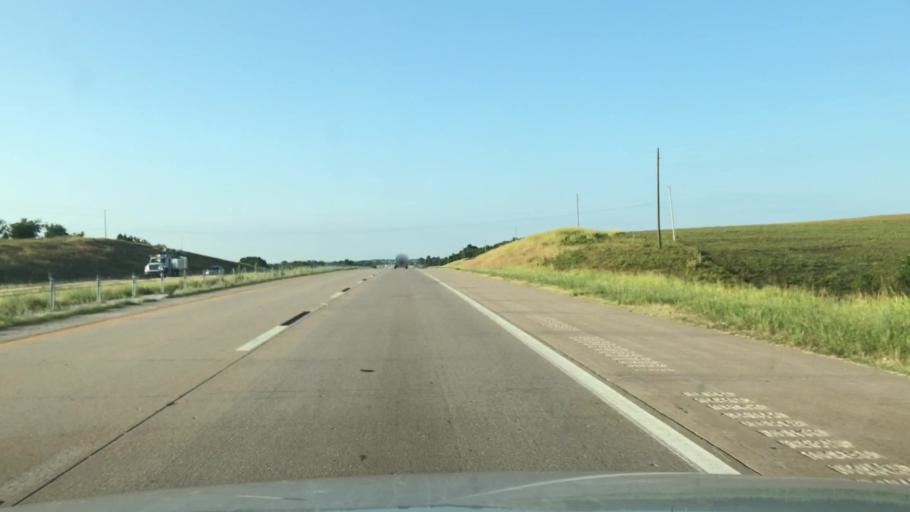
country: US
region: Oklahoma
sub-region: Osage County
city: Skiatook
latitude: 36.4797
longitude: -95.9207
